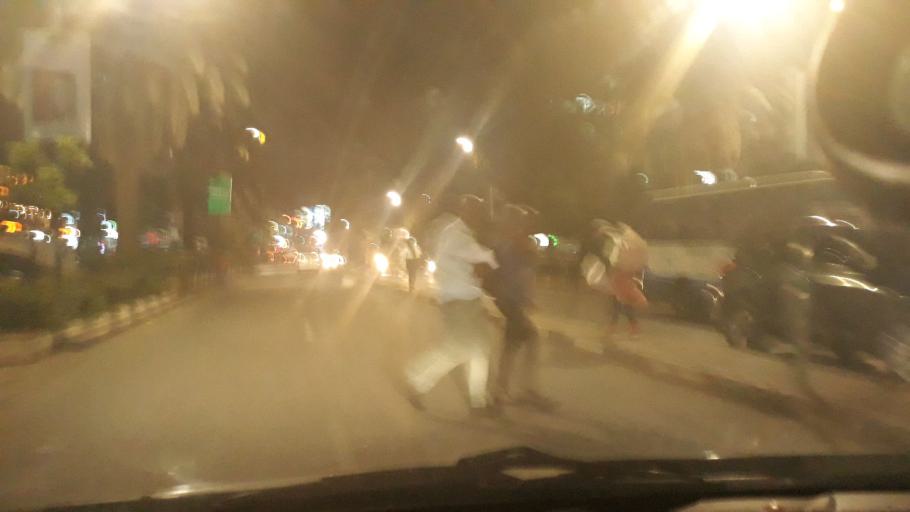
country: KE
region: Nairobi Area
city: Nairobi
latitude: -1.2876
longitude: 36.8267
